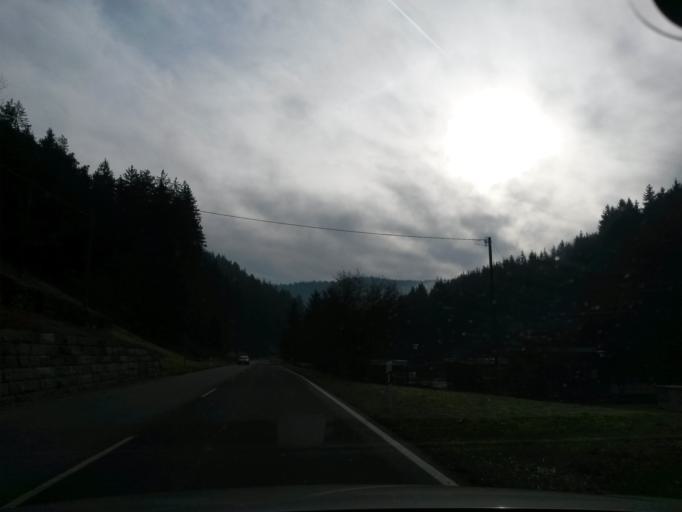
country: DE
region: Baden-Wuerttemberg
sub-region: Freiburg Region
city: Tennenbronn
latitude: 48.1879
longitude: 8.3666
